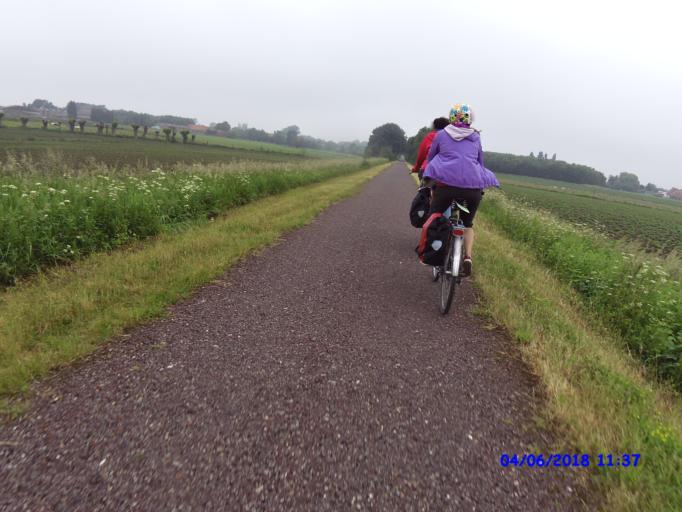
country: BE
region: Flanders
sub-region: Provincie West-Vlaanderen
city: Staden
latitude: 50.9672
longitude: 3.0003
